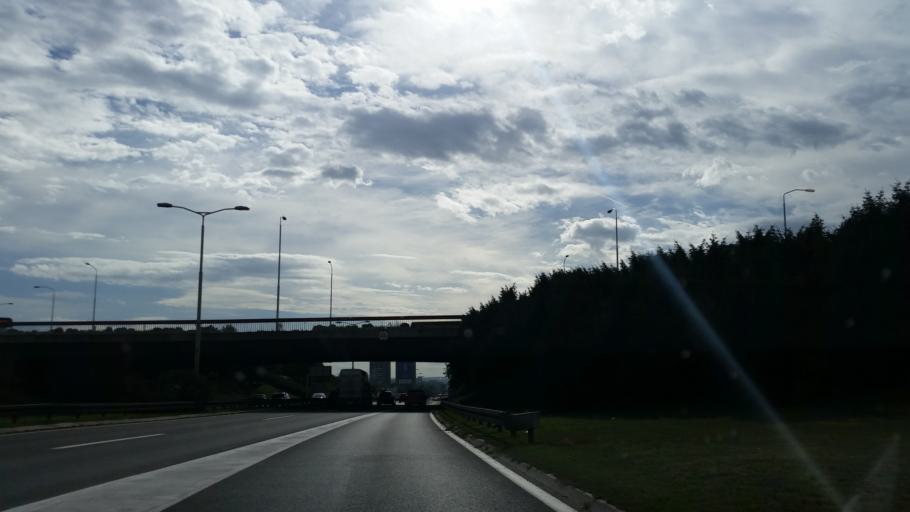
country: RS
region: Central Serbia
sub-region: Belgrade
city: Zemun
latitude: 44.8259
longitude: 20.3904
